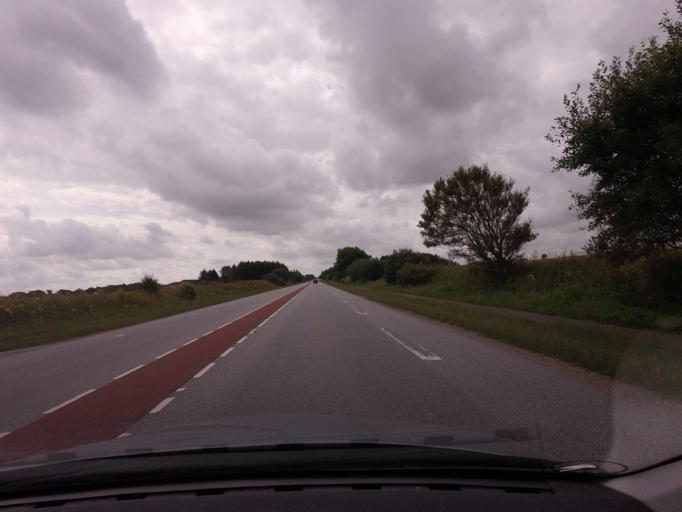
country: DK
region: North Denmark
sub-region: Hjorring Kommune
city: Hjorring
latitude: 57.4094
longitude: 9.9892
